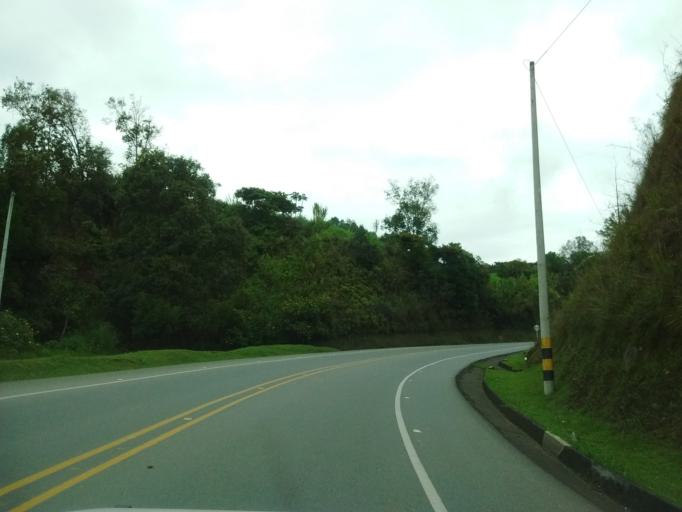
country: CO
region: Cauca
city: Cajibio
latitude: 2.5559
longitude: -76.5662
